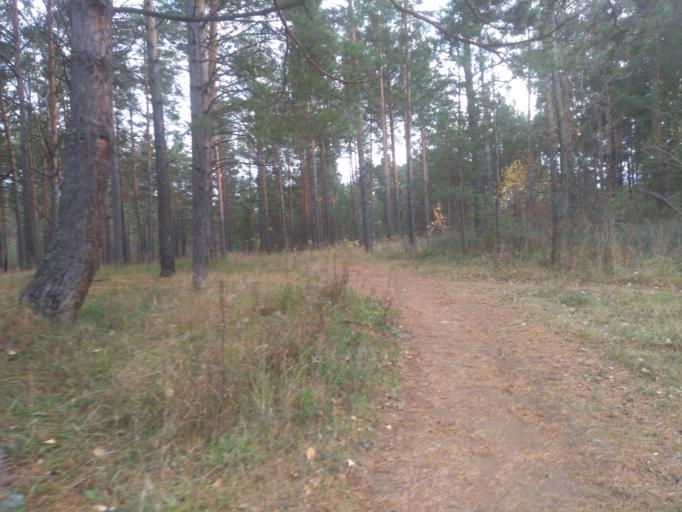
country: RU
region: Tatarstan
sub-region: Tukayevskiy Rayon
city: Naberezhnyye Chelny
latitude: 55.7571
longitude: 52.3781
